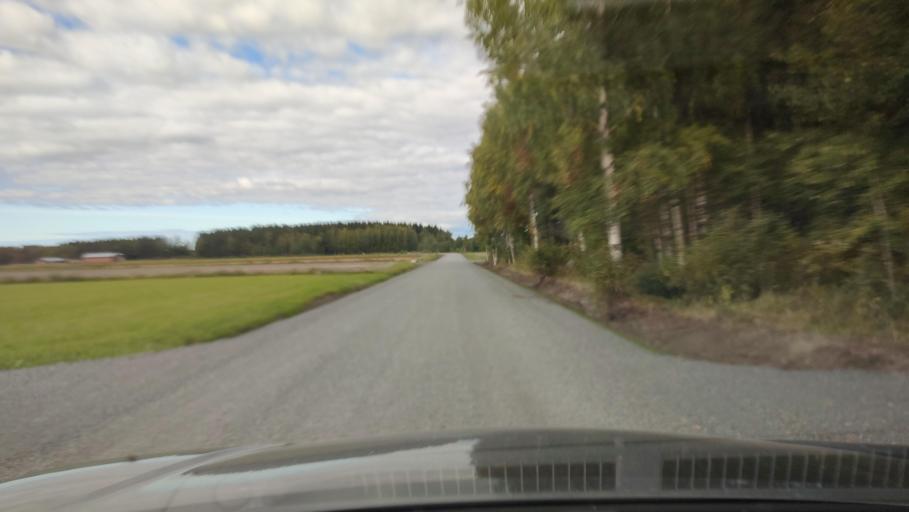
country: FI
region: Southern Ostrobothnia
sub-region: Suupohja
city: Karijoki
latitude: 62.2285
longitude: 21.6189
